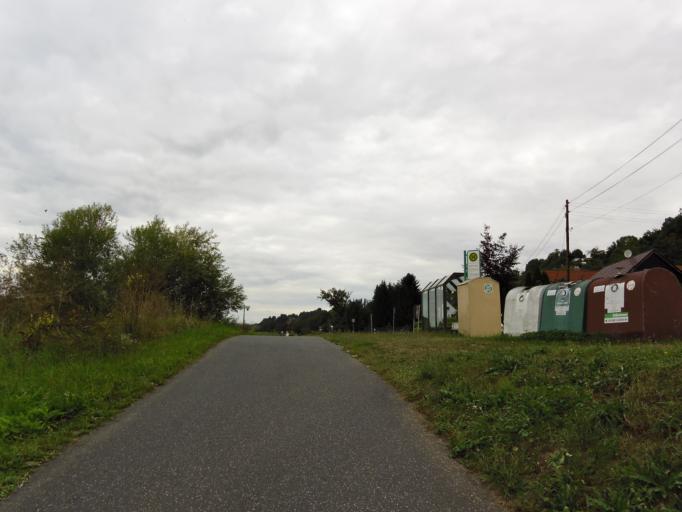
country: DE
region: Saxony
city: Meissen
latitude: 51.1878
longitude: 13.4436
